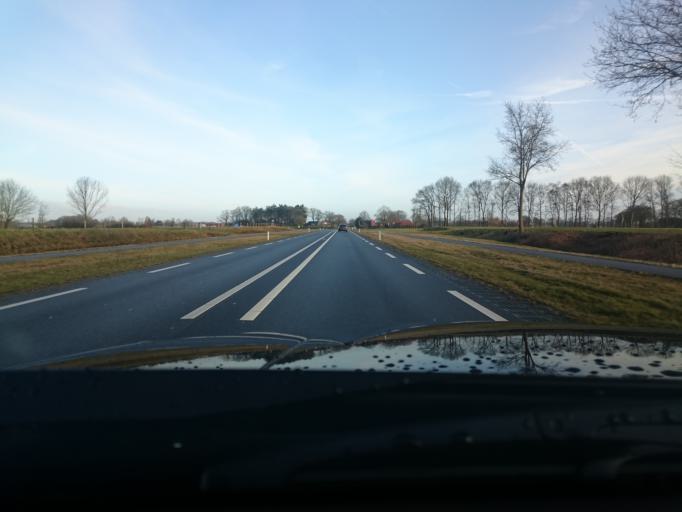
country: NL
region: Overijssel
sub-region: Gemeente Deventer
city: Schalkhaar
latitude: 52.3158
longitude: 6.2058
